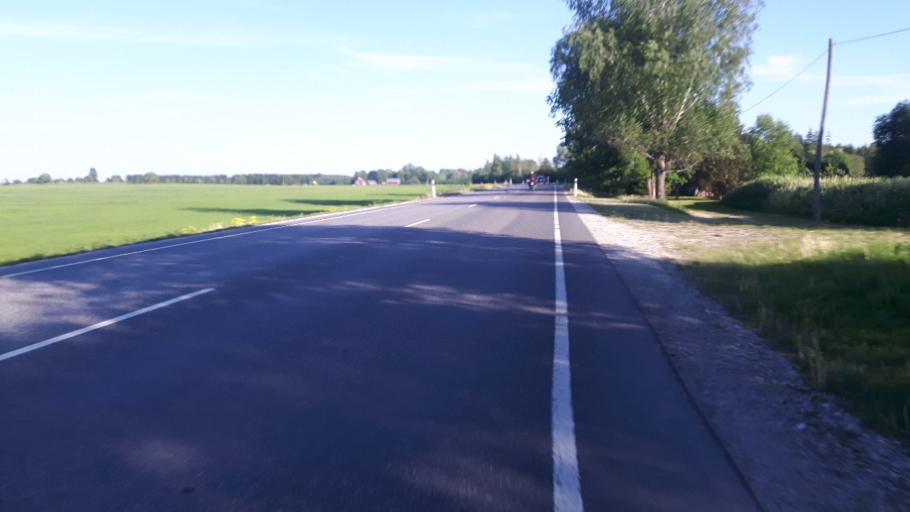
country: EE
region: Raplamaa
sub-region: Kehtna vald
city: Kehtna
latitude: 58.9139
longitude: 24.8796
